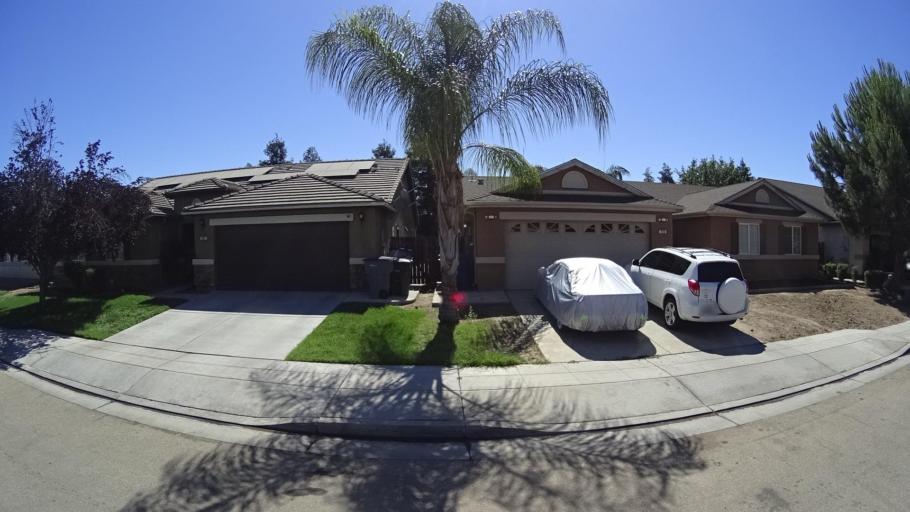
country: US
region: California
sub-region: Fresno County
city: Sunnyside
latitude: 36.7263
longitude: -119.6804
